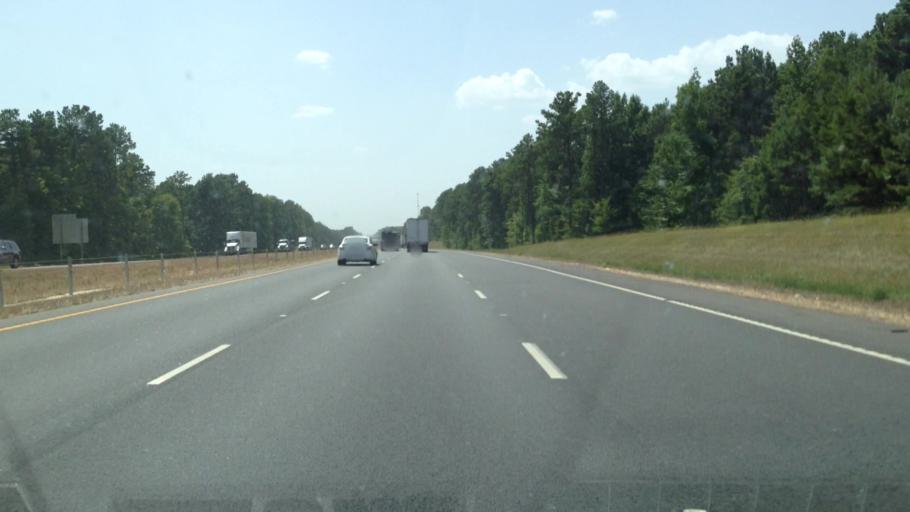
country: US
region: Louisiana
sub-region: Webster Parish
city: Minden
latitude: 32.5719
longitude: -93.2069
